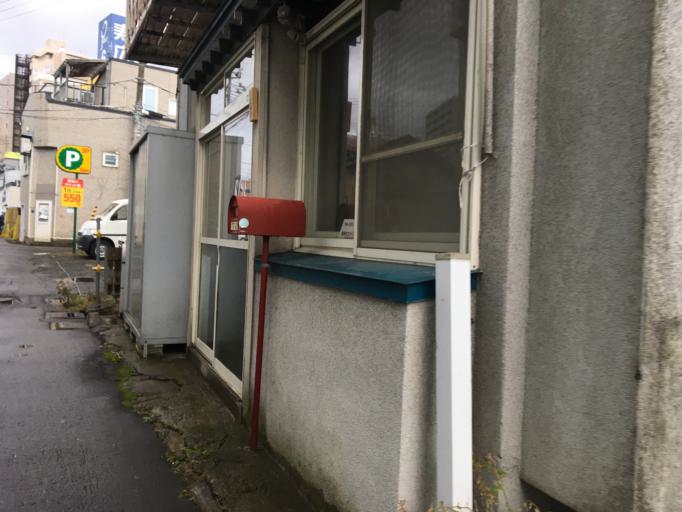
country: JP
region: Aomori
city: Aomori Shi
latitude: 40.8259
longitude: 140.7341
